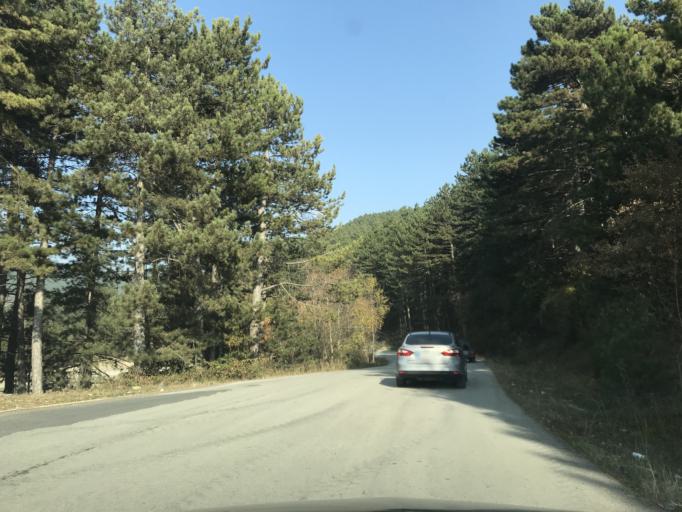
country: TR
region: Bolu
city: Bolu
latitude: 40.7807
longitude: 31.6322
